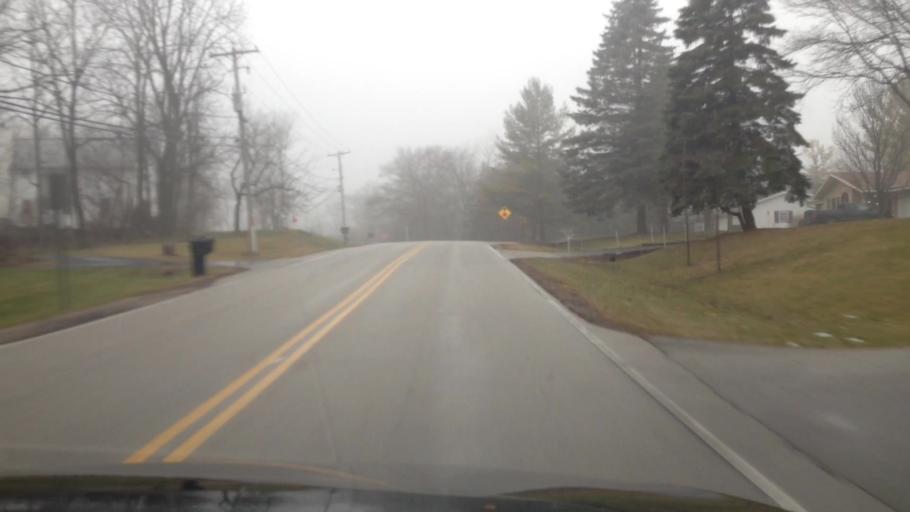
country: US
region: Wisconsin
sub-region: Milwaukee County
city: Hales Corners
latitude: 42.9238
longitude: -88.0604
